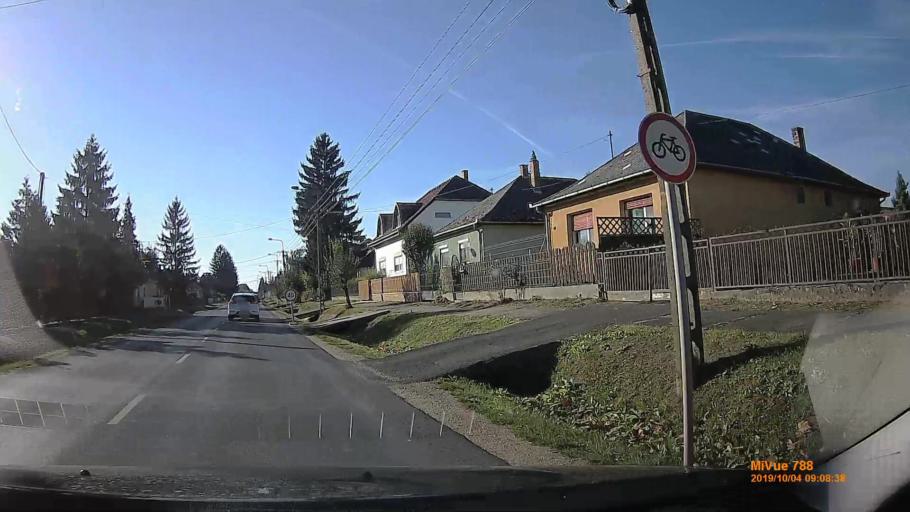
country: HU
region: Somogy
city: Karad
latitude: 46.6693
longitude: 17.7781
